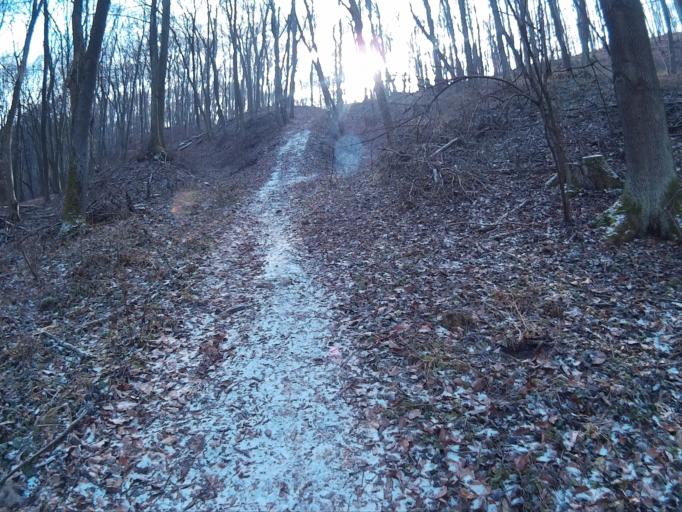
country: HU
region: Komarom-Esztergom
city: Tatabanya
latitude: 47.5124
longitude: 18.4137
